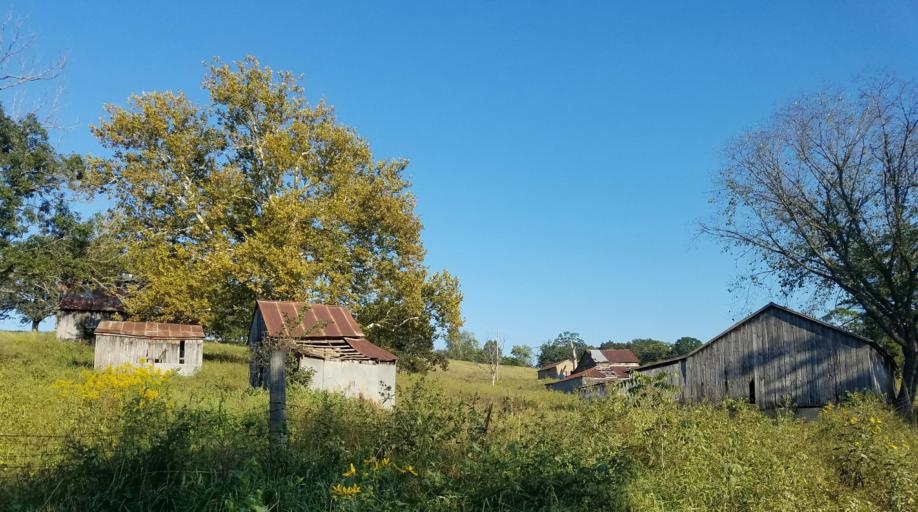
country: US
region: Missouri
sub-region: Moniteau County
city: California
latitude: 38.7268
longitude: -92.6107
